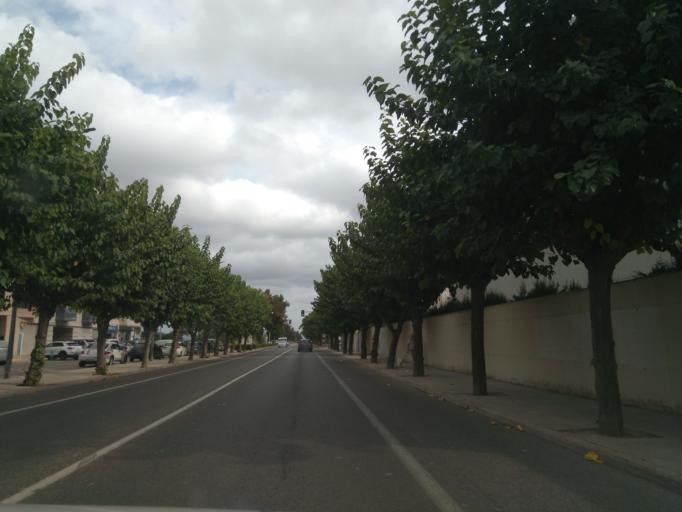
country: ES
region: Valencia
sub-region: Provincia de Valencia
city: Carlet
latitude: 39.2210
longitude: -0.5185
